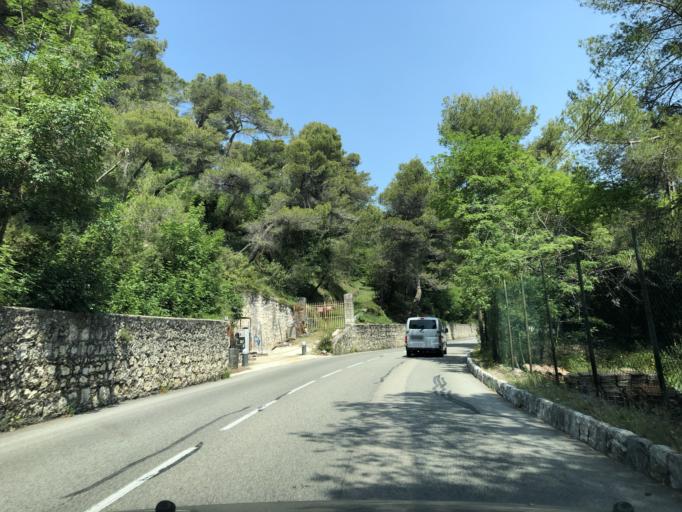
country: FR
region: Provence-Alpes-Cote d'Azur
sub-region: Departement des Alpes-Maritimes
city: La Trinite
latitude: 43.7279
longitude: 7.3029
